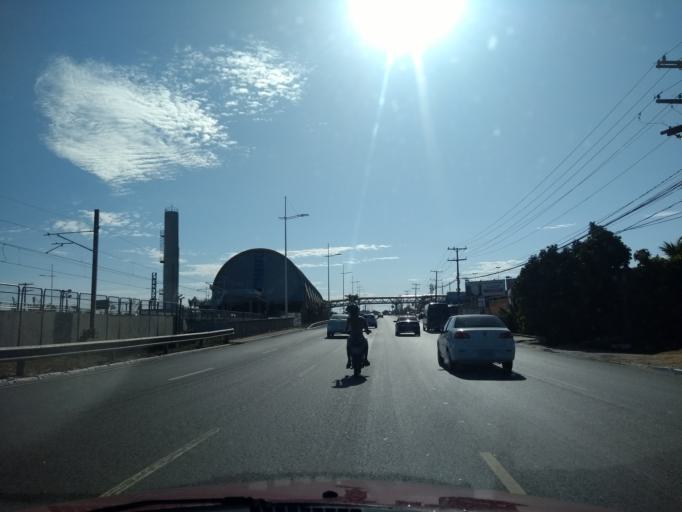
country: BR
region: Bahia
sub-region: Lauro De Freitas
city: Lauro de Freitas
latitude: -12.9209
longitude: -38.3573
